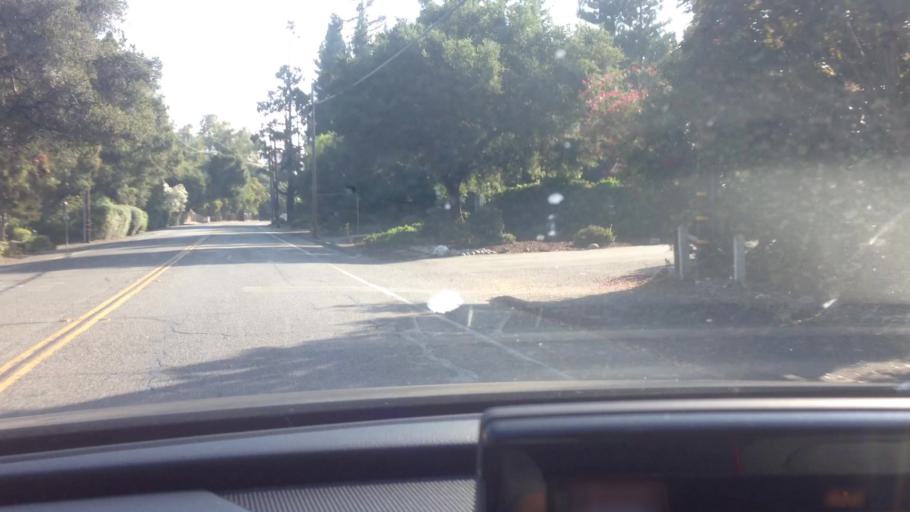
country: US
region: California
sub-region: Santa Clara County
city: Saratoga
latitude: 37.2671
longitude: -122.0203
